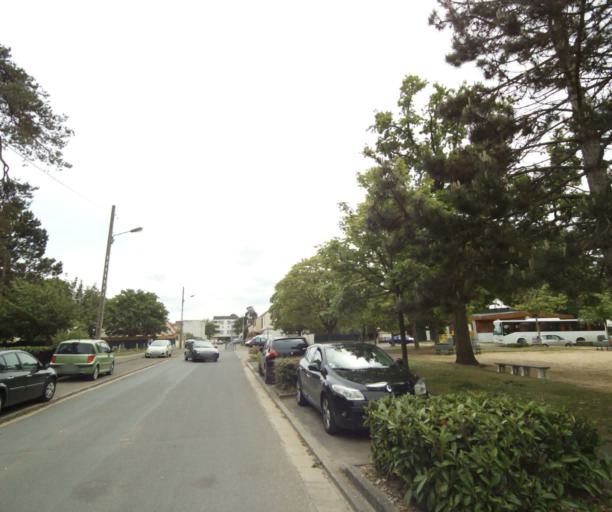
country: FR
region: Ile-de-France
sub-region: Departement des Yvelines
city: Les Mureaux
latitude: 48.9867
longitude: 1.9270
